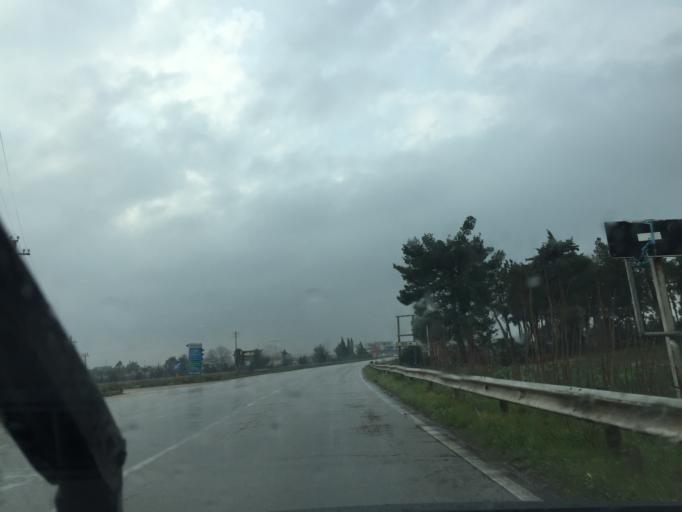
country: IT
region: Apulia
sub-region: Provincia di Foggia
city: Foggia
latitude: 41.4912
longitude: 15.5228
